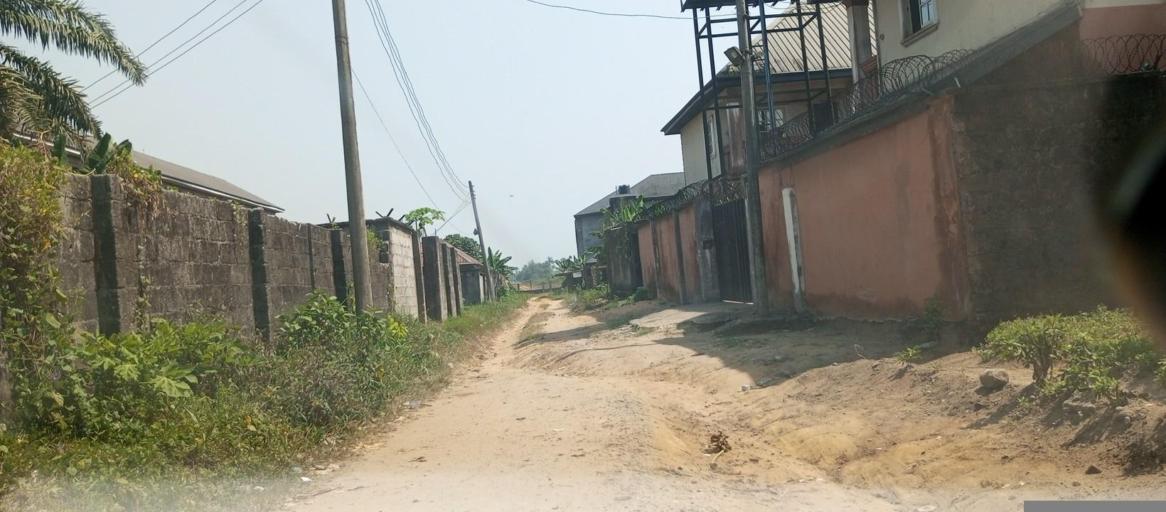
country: NG
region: Rivers
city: Emuoha
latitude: 4.9182
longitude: 6.9197
